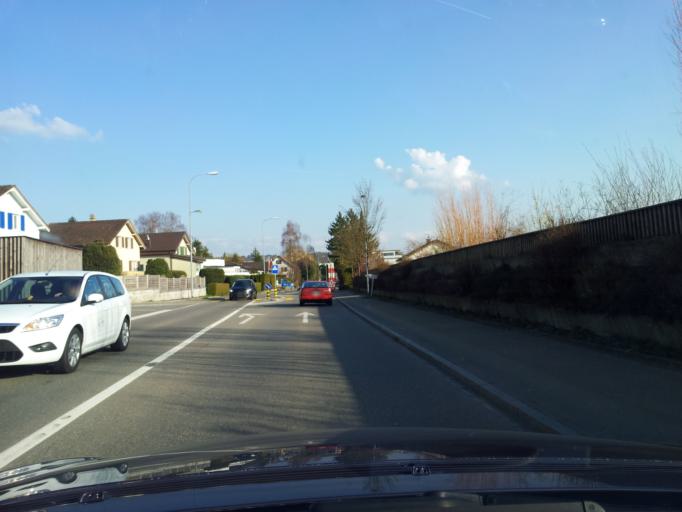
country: CH
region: Aargau
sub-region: Bezirk Bremgarten
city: Rudolfstetten
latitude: 47.3693
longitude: 8.3606
